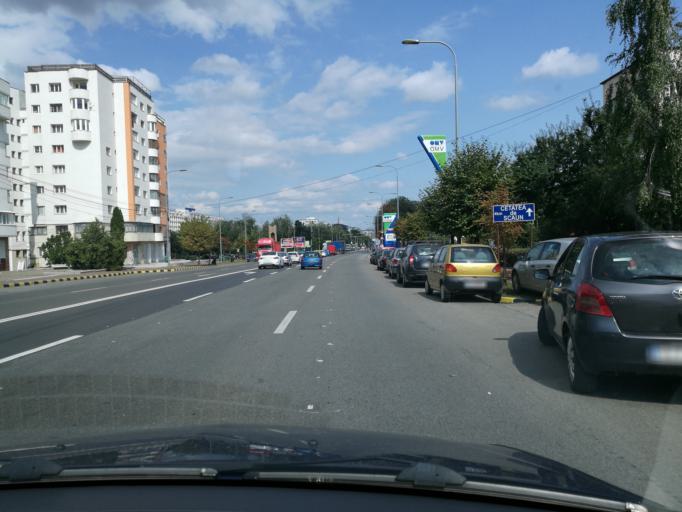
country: RO
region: Suceava
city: Suceava
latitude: 47.6363
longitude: 26.2364
